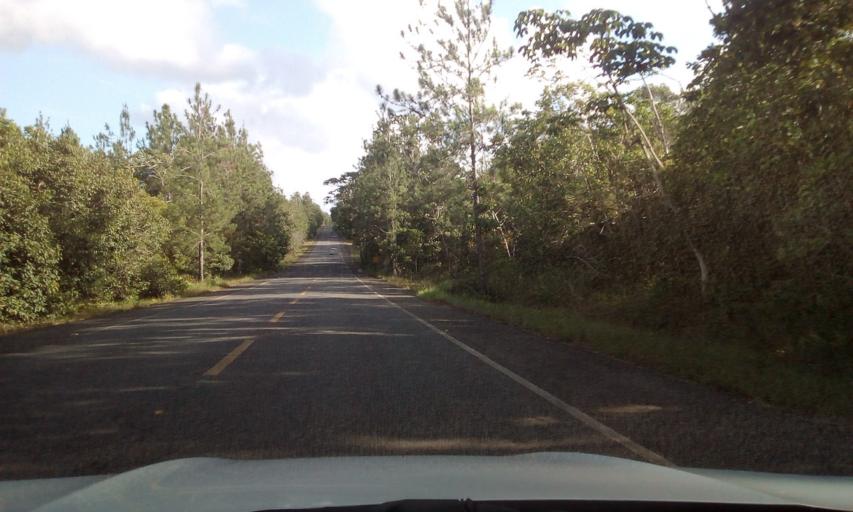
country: BR
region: Bahia
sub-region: Entre Rios
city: Entre Rios
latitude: -12.1101
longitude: -37.7850
